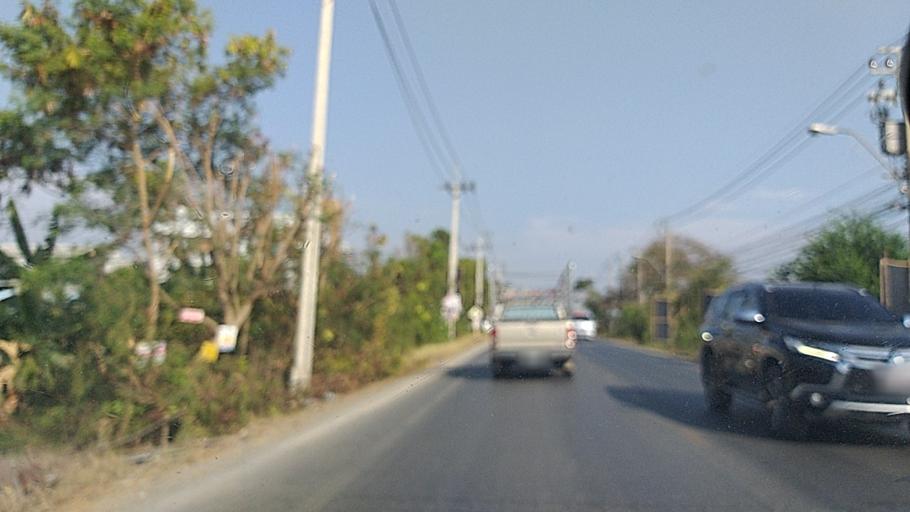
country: TH
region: Nonthaburi
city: Bang Bua Thong
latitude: 13.9343
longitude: 100.3715
